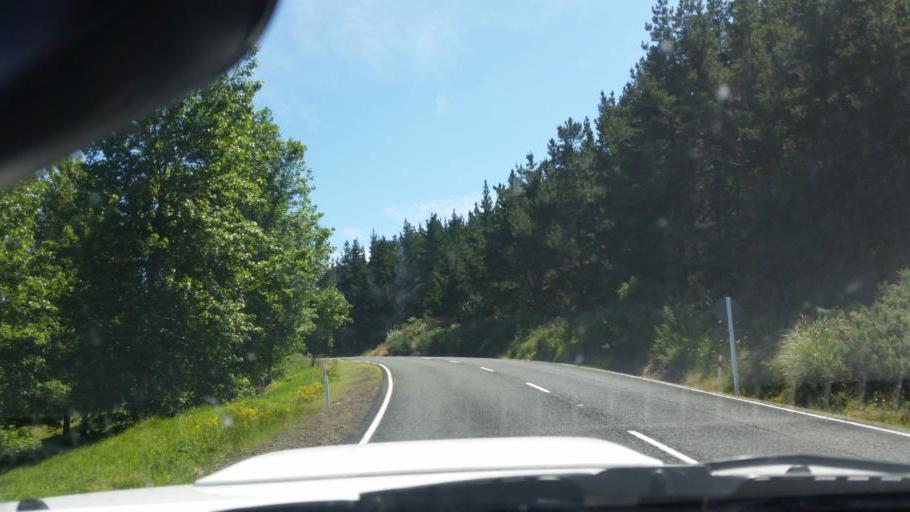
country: NZ
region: Auckland
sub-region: Auckland
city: Wellsford
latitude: -36.2073
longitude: 174.3928
